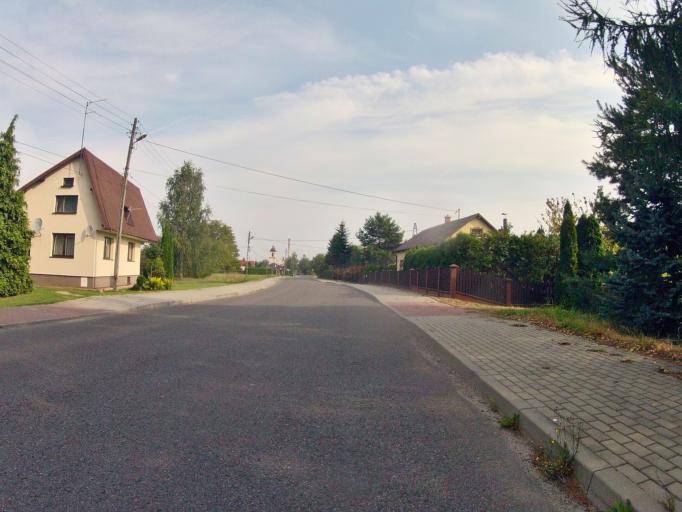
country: PL
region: Subcarpathian Voivodeship
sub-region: Powiat jasielski
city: Debowiec
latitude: 49.7149
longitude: 21.4616
